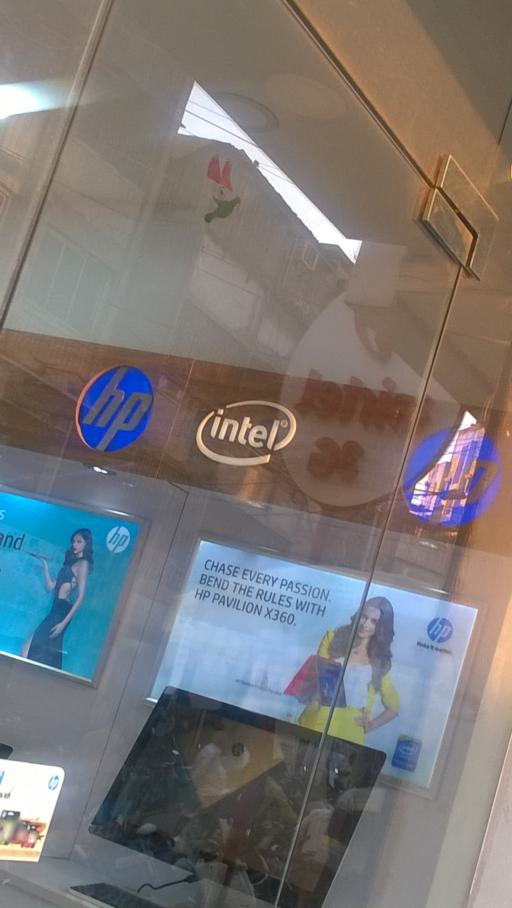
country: IN
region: Maharashtra
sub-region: Thane
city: Ulhasnagar
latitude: 19.2294
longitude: 73.1602
